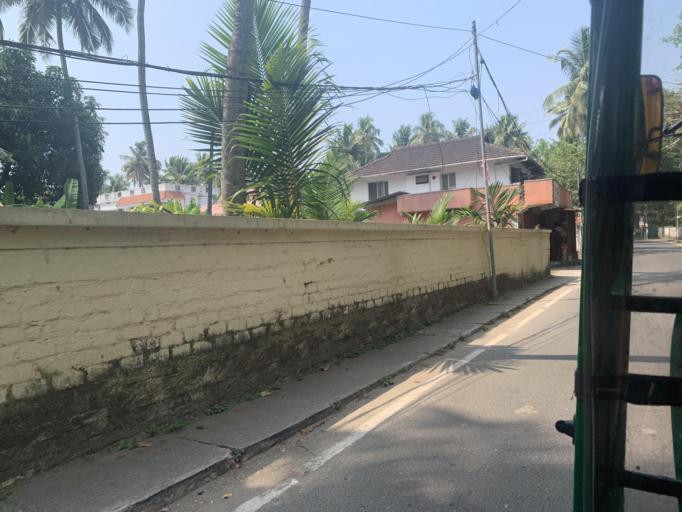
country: IN
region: Kerala
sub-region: Ernakulam
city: Cochin
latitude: 9.9418
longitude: 76.3014
